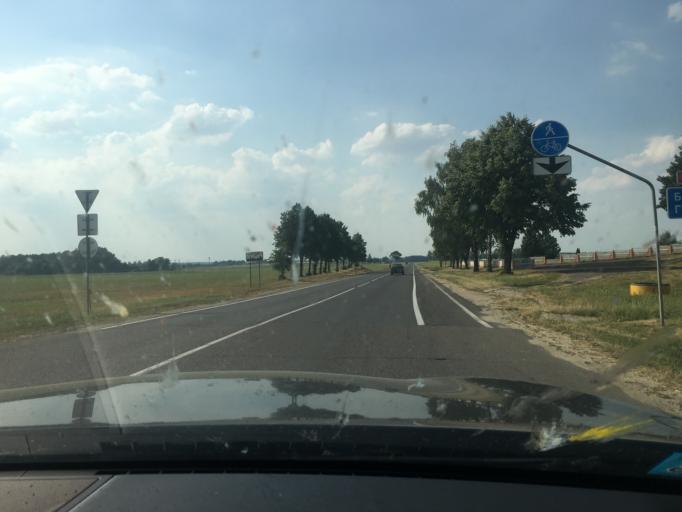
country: BY
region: Grodnenskaya
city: Svislach
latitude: 53.0431
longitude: 24.0854
